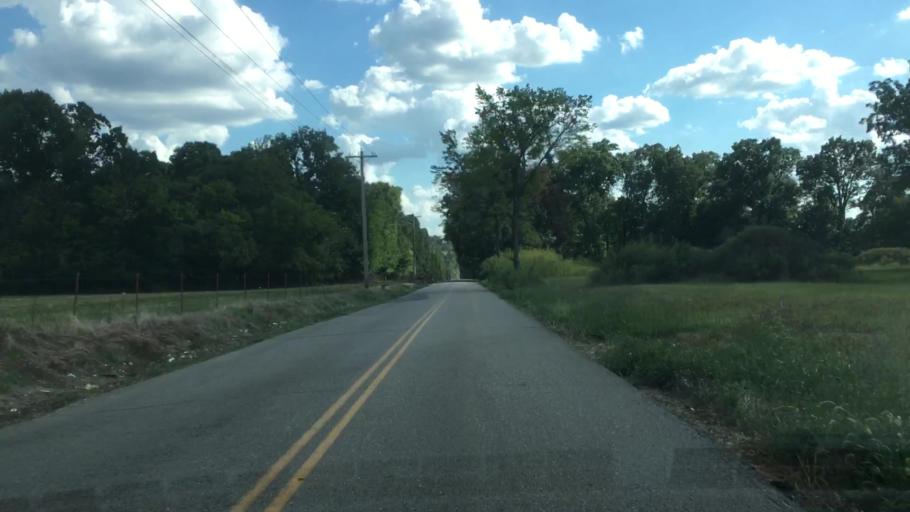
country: US
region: Oklahoma
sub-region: Cherokee County
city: Park Hill
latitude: 35.8049
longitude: -95.0739
